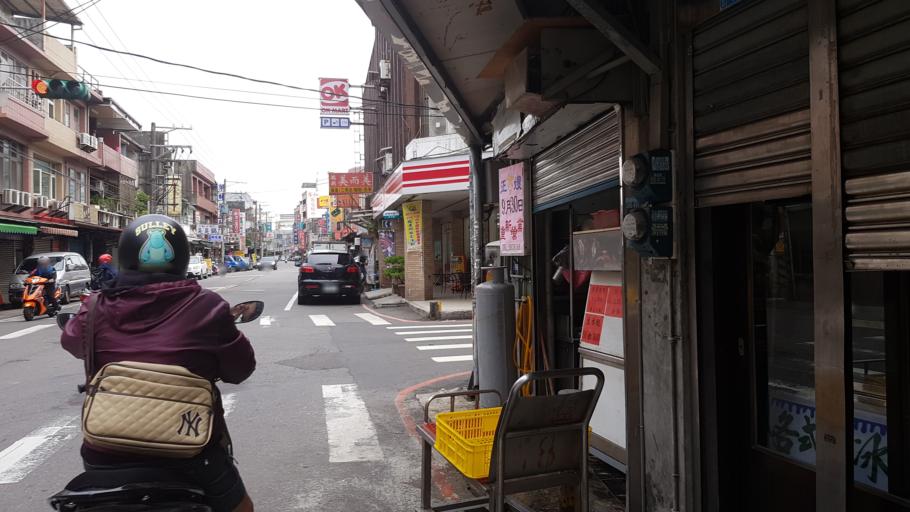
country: TW
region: Taiwan
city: Taoyuan City
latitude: 25.0782
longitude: 121.2575
